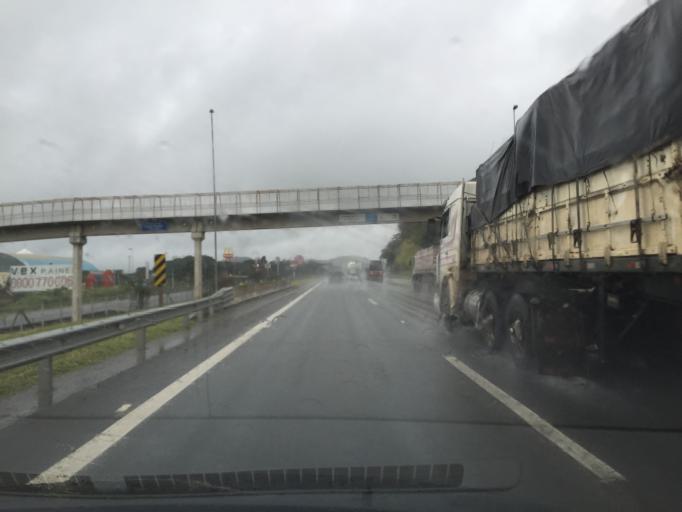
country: BR
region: Sao Paulo
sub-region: Itu
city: Itu
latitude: -23.4092
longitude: -47.2824
